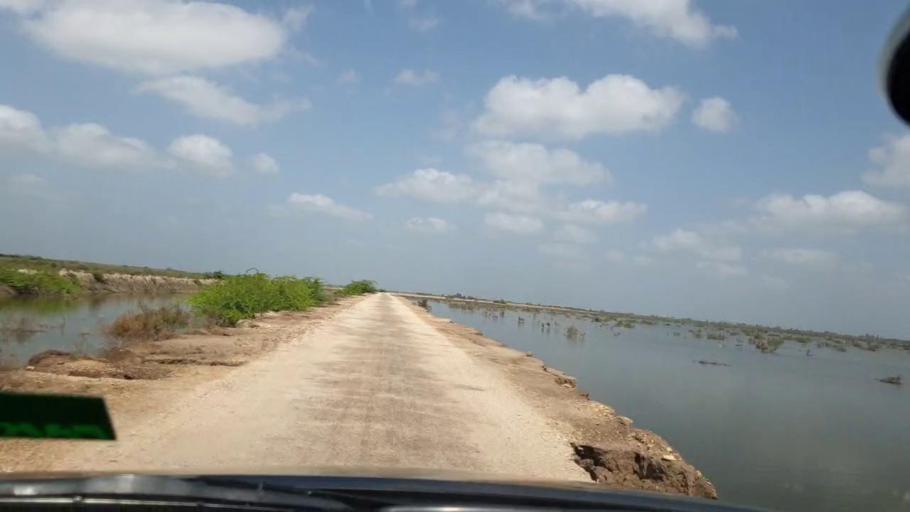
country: PK
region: Sindh
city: Kadhan
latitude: 24.5804
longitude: 69.1411
